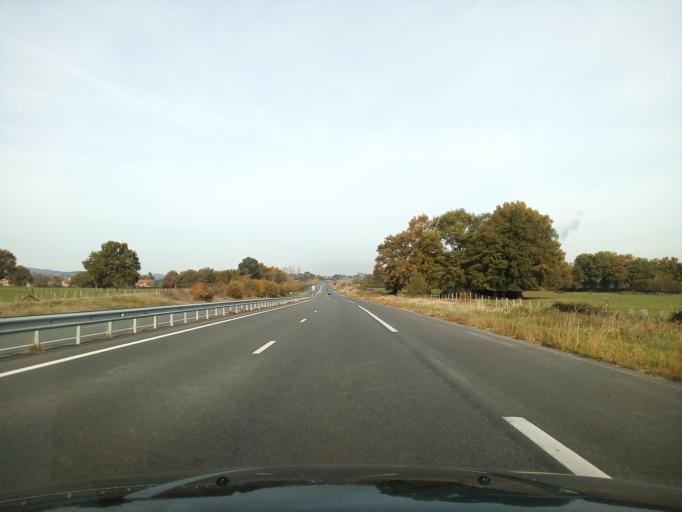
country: FR
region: Rhone-Alpes
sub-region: Departement de la Loire
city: La Pacaudiere
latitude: 46.1637
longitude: 3.8885
